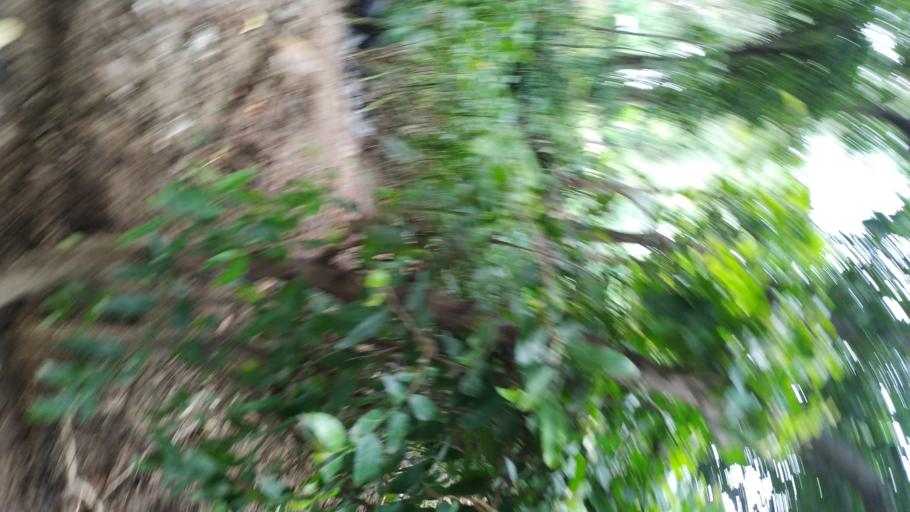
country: IN
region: NCT
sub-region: New Delhi
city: New Delhi
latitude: 28.5698
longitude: 77.2488
